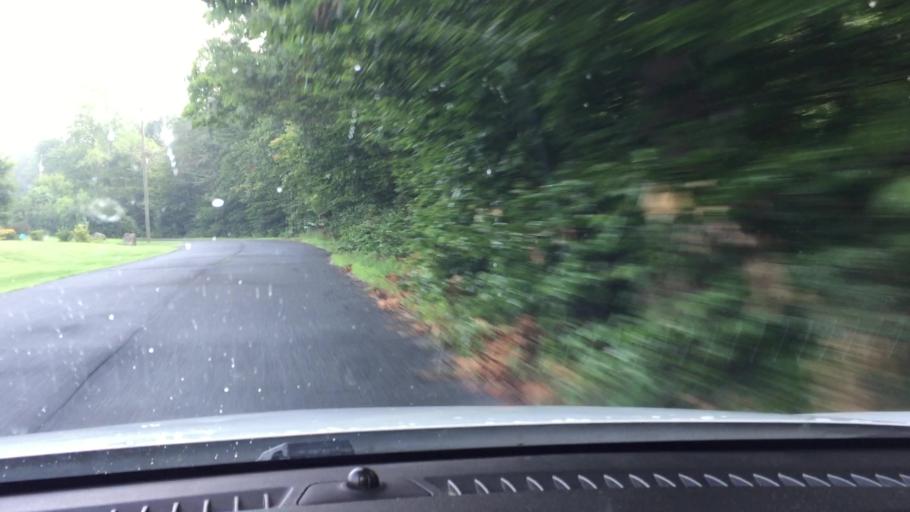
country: US
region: Massachusetts
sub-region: Berkshire County
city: Becket
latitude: 42.3565
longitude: -72.9639
